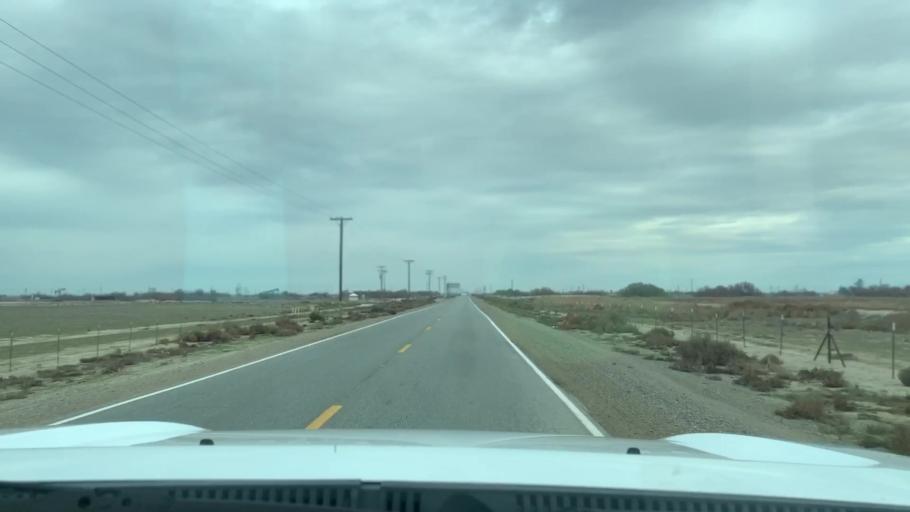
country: US
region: California
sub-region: Kern County
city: Rosedale
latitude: 35.3147
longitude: -119.2524
